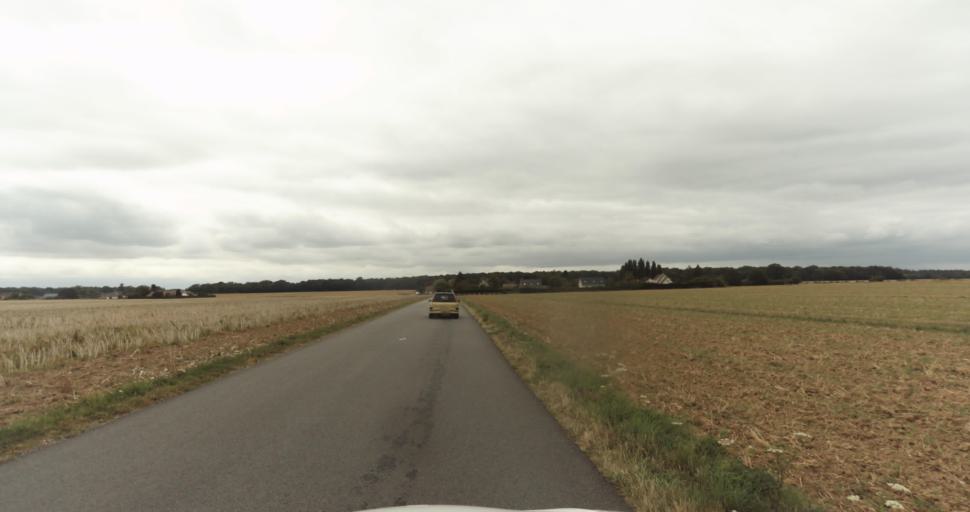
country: FR
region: Haute-Normandie
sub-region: Departement de l'Eure
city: Arnieres-sur-Iton
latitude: 48.9586
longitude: 1.1217
